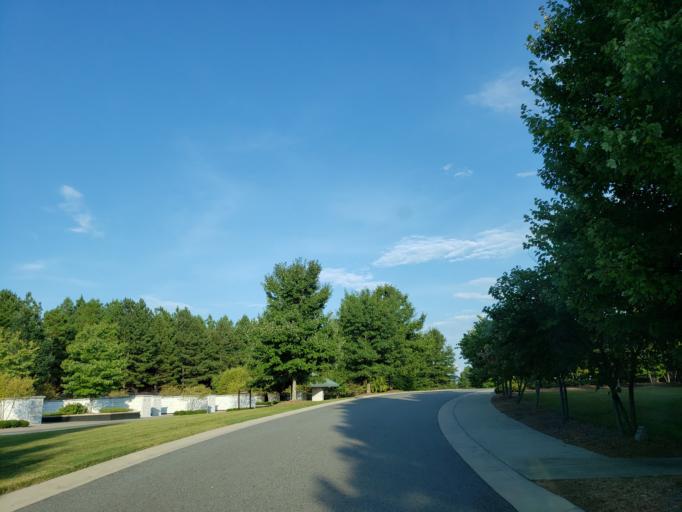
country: US
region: Georgia
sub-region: Cherokee County
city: Canton
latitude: 34.2352
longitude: -84.5811
